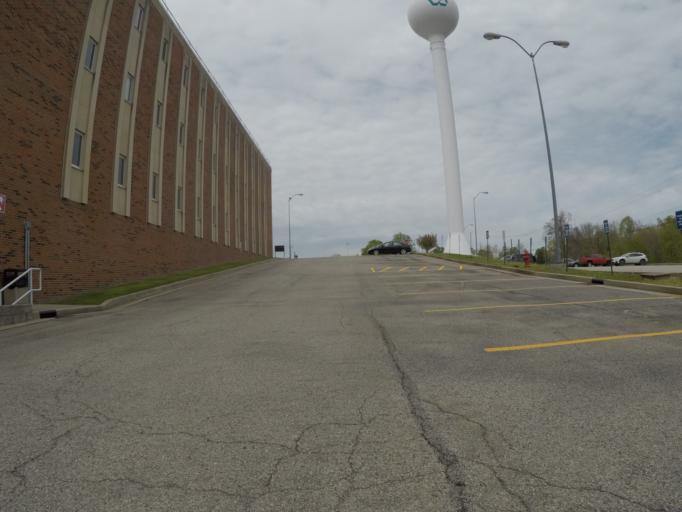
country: US
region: Ohio
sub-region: Lawrence County
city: Burlington
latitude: 38.3768
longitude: -82.5156
